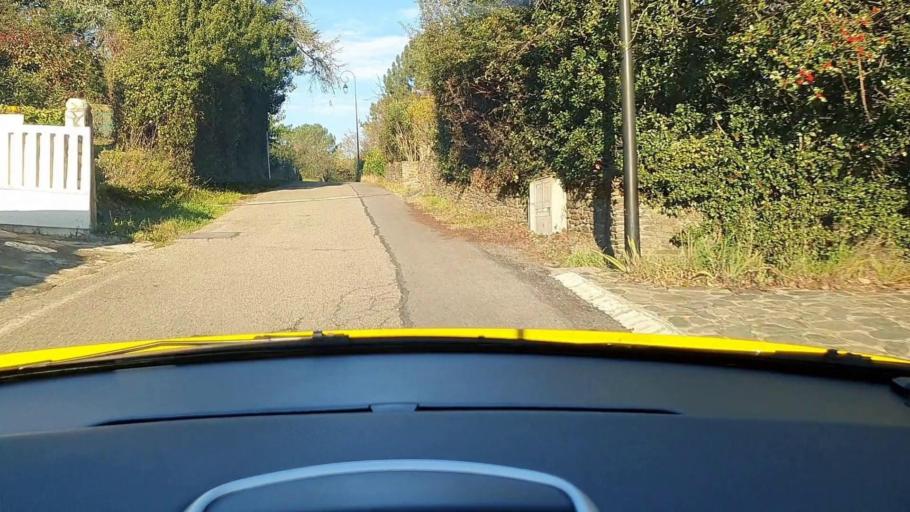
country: FR
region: Languedoc-Roussillon
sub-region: Departement du Gard
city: Branoux-les-Taillades
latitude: 44.2277
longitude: 4.0086
